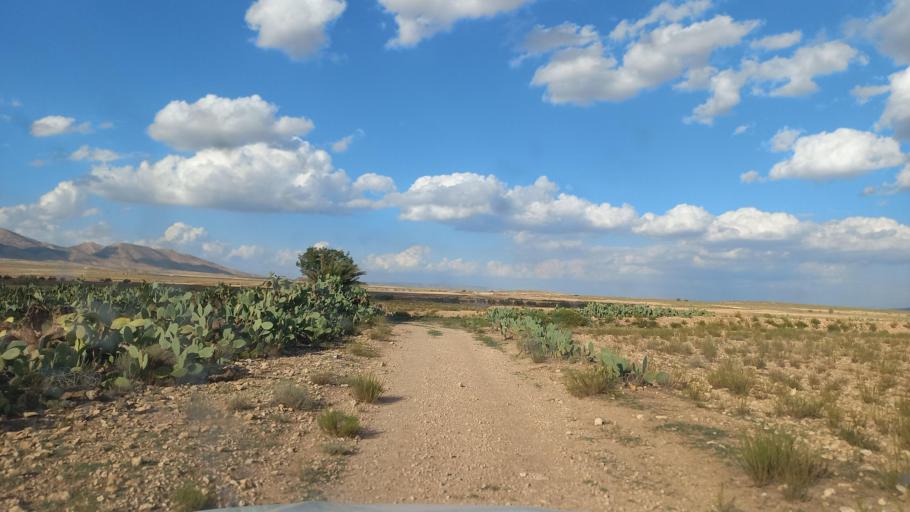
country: TN
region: Al Qasrayn
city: Sbiba
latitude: 35.3920
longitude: 9.0441
